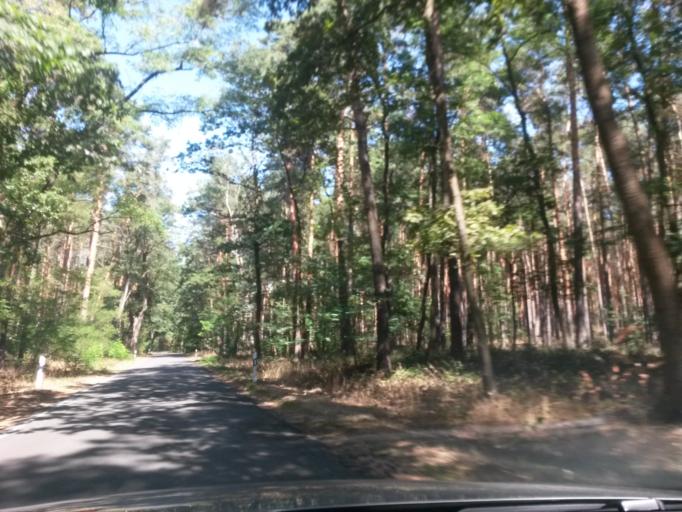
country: DE
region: Saxony-Anhalt
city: Pretzsch
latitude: 51.7534
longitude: 12.8464
